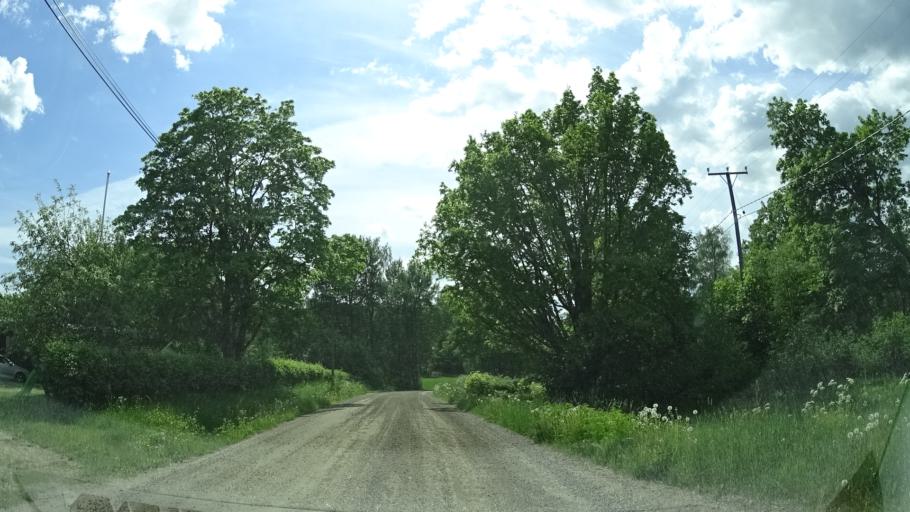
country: FI
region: Uusimaa
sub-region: Helsinki
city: Siuntio
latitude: 60.2190
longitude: 24.2943
